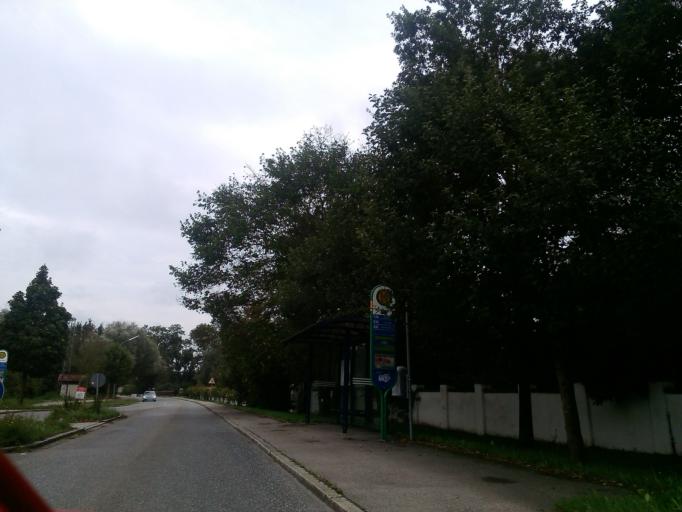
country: DE
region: Bavaria
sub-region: Upper Bavaria
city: Olching
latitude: 48.2256
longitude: 11.3427
